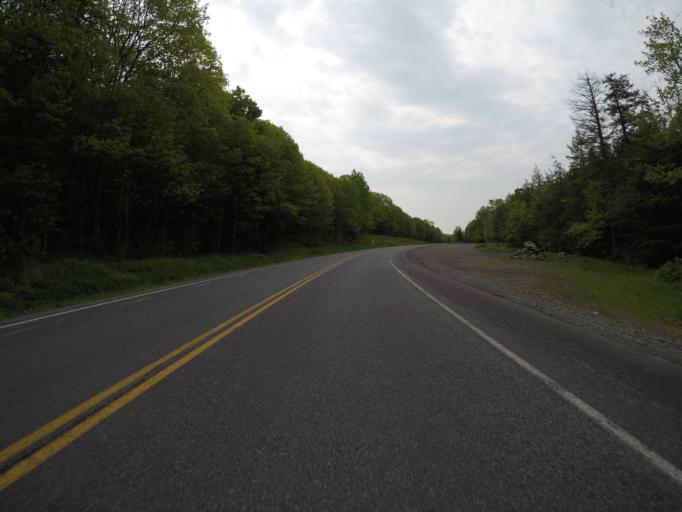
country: US
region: New York
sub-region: Sullivan County
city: Livingston Manor
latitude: 42.0362
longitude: -74.9001
